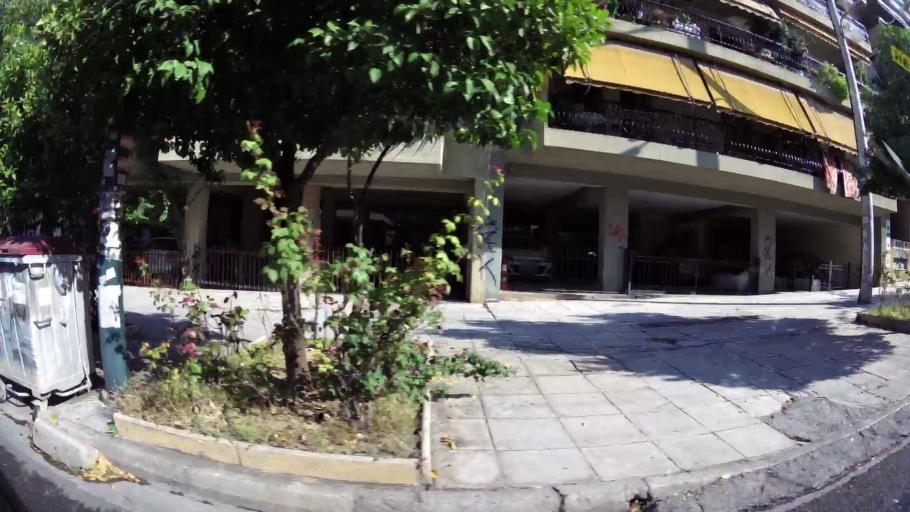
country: GR
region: Attica
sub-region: Nomarchia Athinas
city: Galatsi
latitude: 38.0208
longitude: 23.7448
